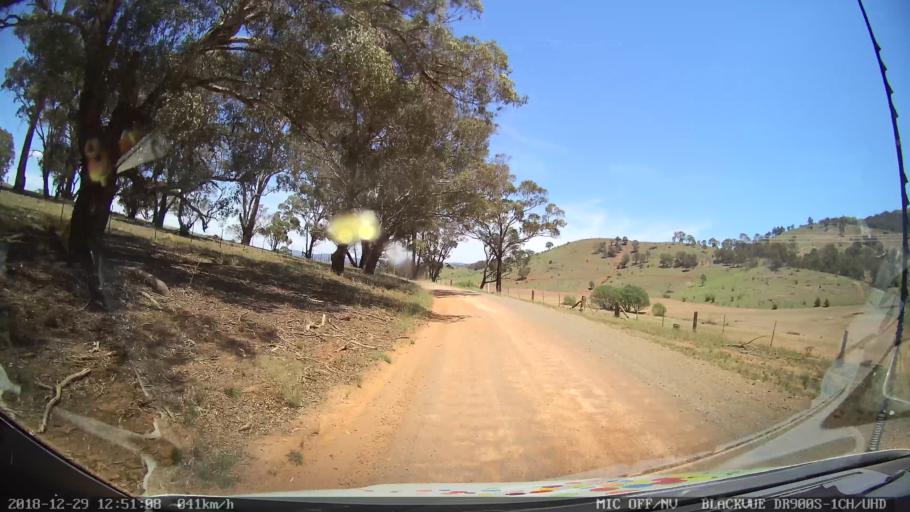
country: AU
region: Australian Capital Territory
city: Macarthur
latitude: -35.6733
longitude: 149.2002
